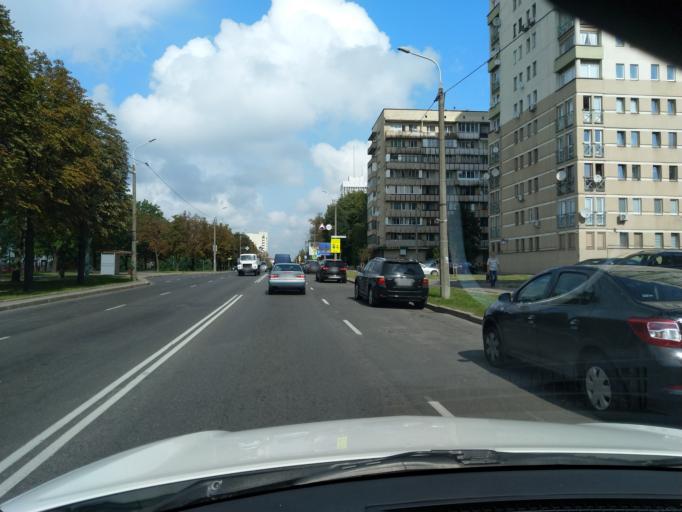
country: BY
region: Minsk
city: Minsk
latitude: 53.8977
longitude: 27.5872
